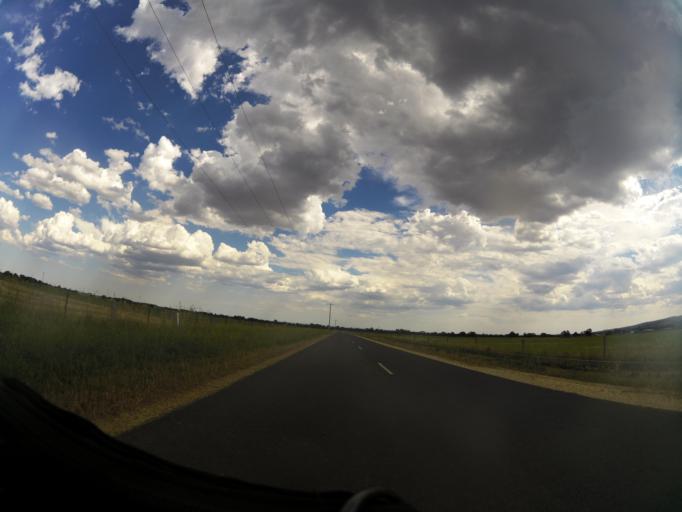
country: AU
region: Victoria
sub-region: Wellington
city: Heyfield
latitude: -37.9919
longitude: 146.6927
